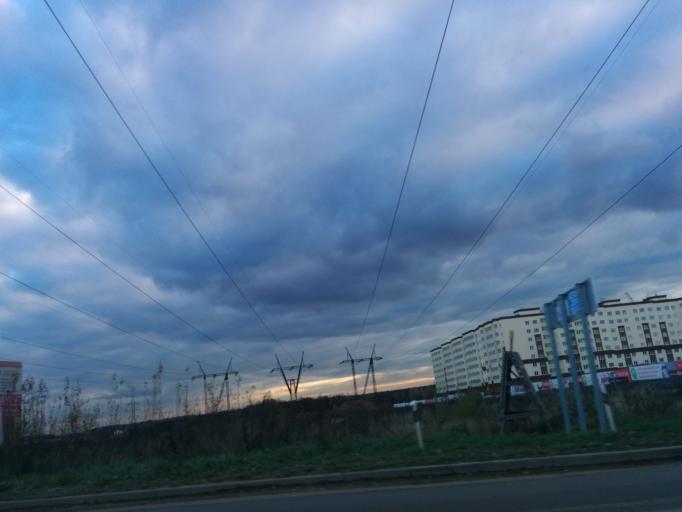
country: RU
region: Moscow
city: Zagor'ye
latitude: 55.5372
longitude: 37.6392
